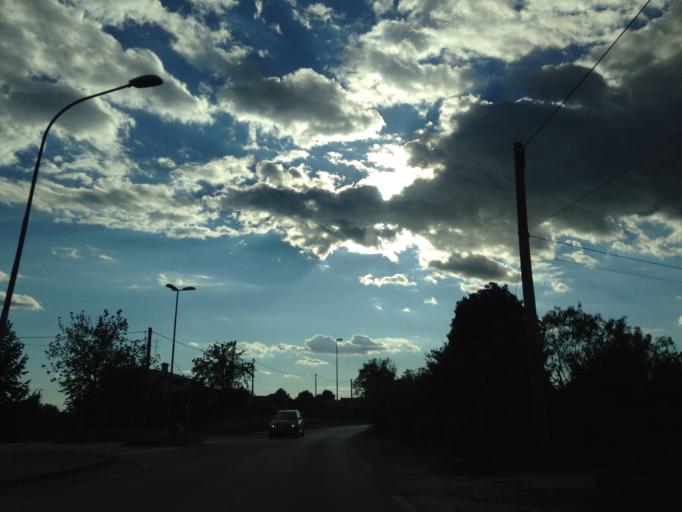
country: IT
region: Friuli Venezia Giulia
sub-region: Provincia di Pordenone
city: Sacile
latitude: 45.9532
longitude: 12.5362
